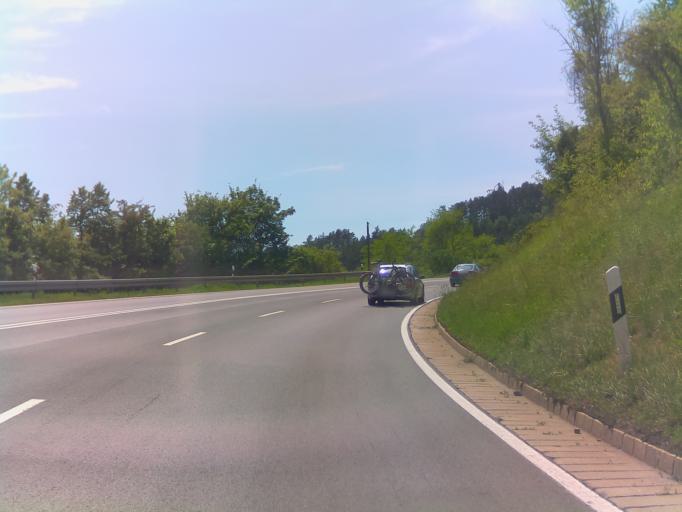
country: DE
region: Bavaria
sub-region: Regierungsbezirk Unterfranken
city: Munnerstadt
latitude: 50.2420
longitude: 10.1917
